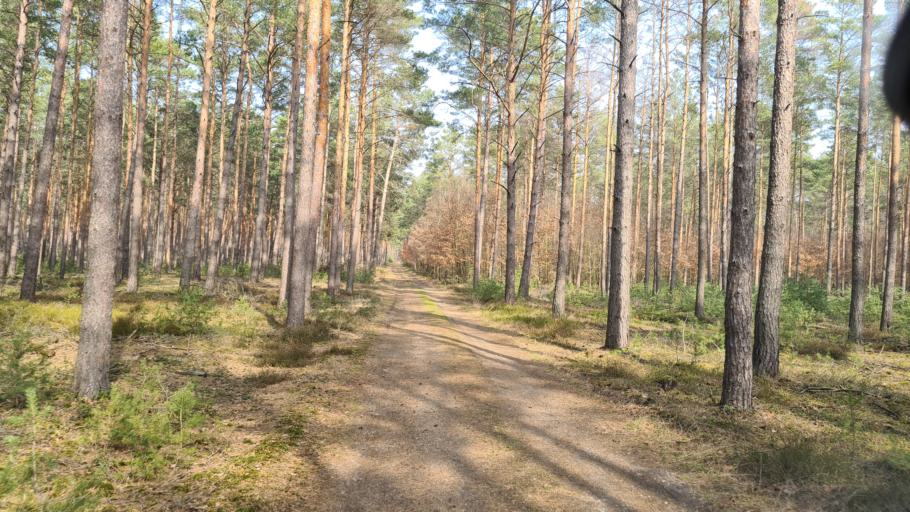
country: DE
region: Brandenburg
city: Trobitz
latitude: 51.6507
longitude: 13.4582
